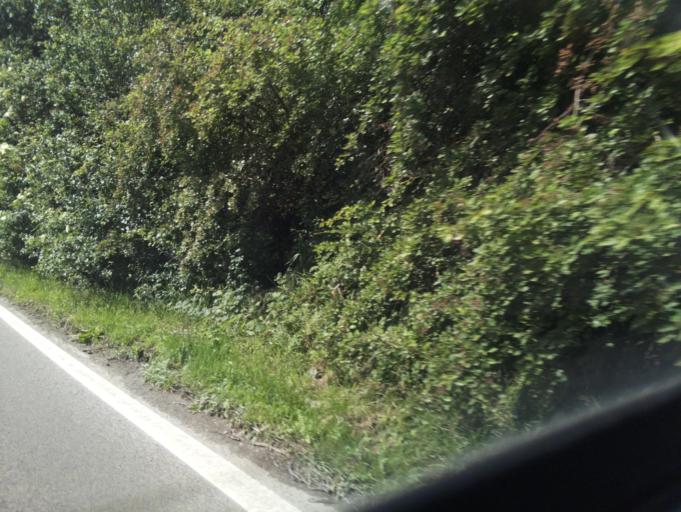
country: GB
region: England
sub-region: North Lincolnshire
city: Manton
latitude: 53.5093
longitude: -0.5823
